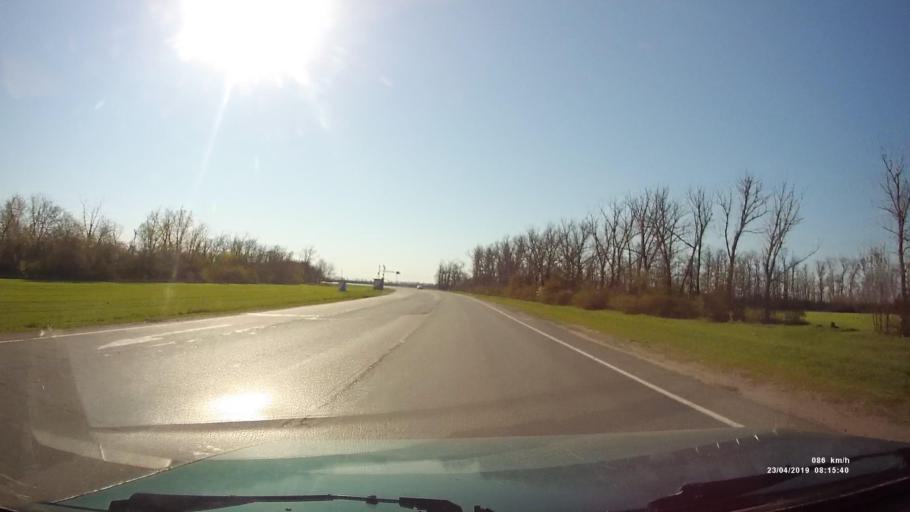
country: RU
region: Rostov
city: Yegorlykskaya
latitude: 46.5381
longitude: 40.7776
